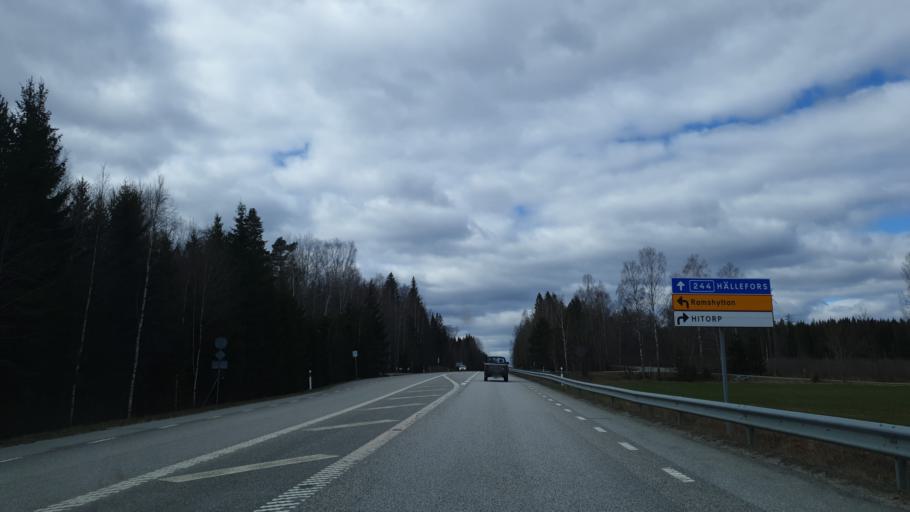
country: SE
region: OErebro
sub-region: Nora Kommun
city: Nora
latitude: 59.4927
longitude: 15.0539
